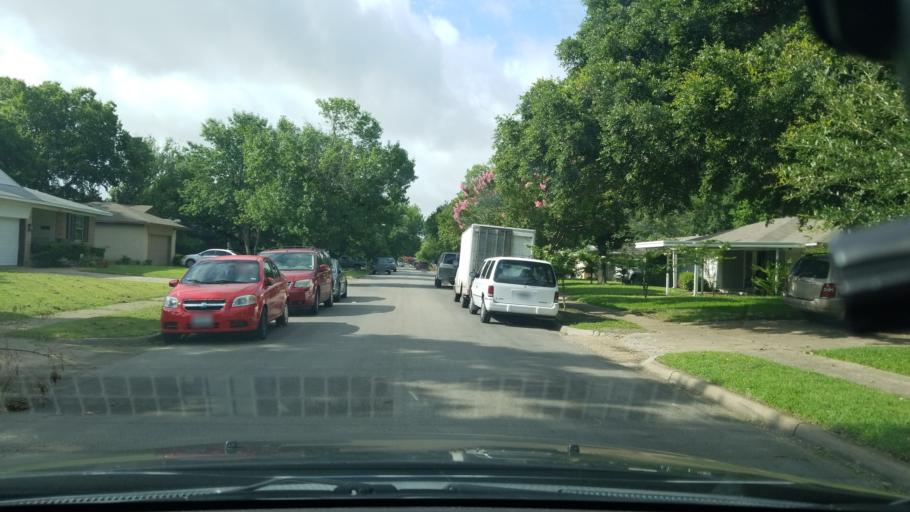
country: US
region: Texas
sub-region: Dallas County
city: Mesquite
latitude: 32.8172
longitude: -96.6766
